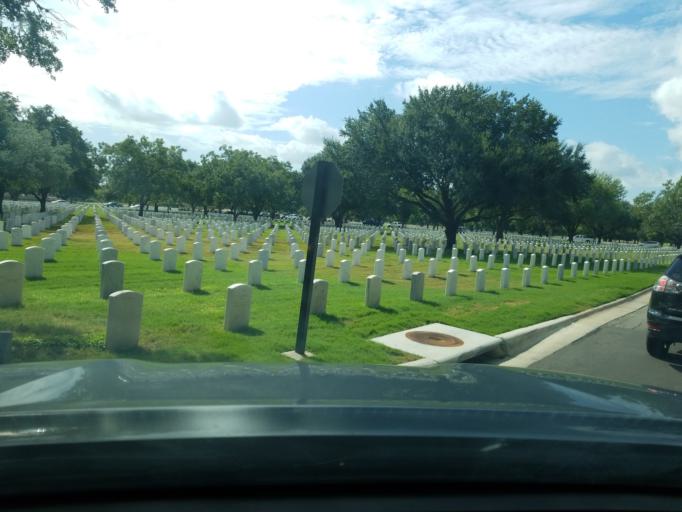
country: US
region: Texas
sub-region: Bexar County
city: Terrell Hills
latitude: 29.4768
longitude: -98.4301
